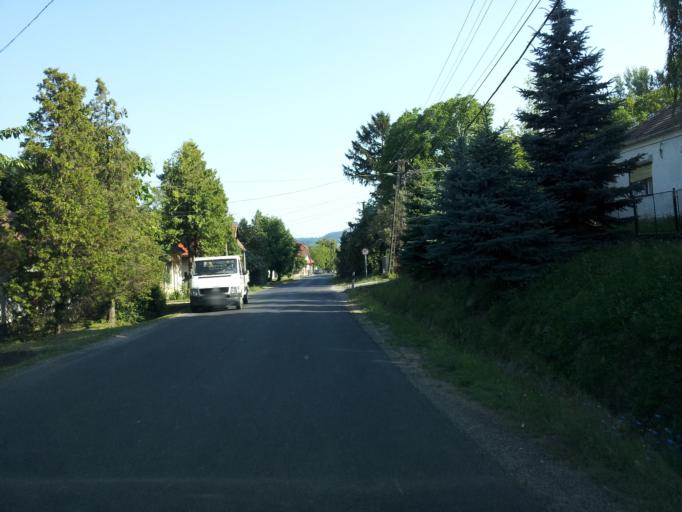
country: HU
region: Zala
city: Gyenesdias
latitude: 46.8619
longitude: 17.2983
